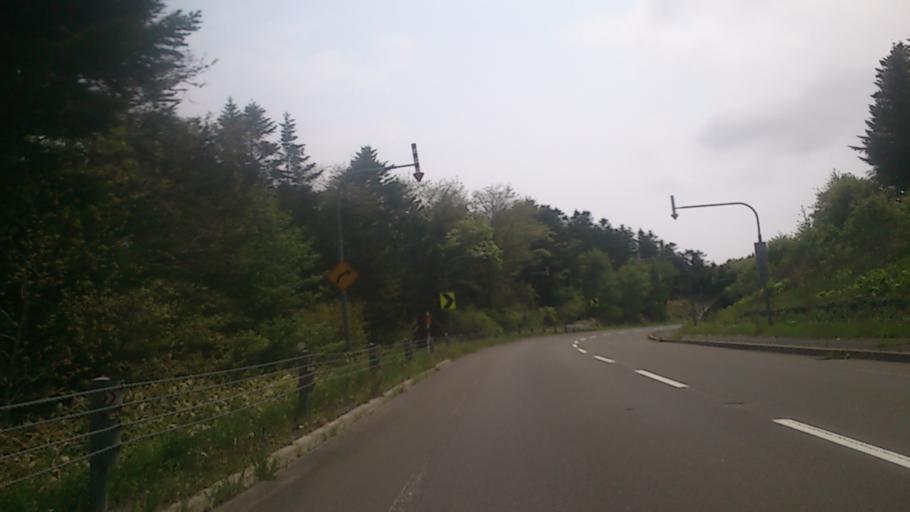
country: JP
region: Hokkaido
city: Nemuro
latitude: 43.2755
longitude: 145.5539
